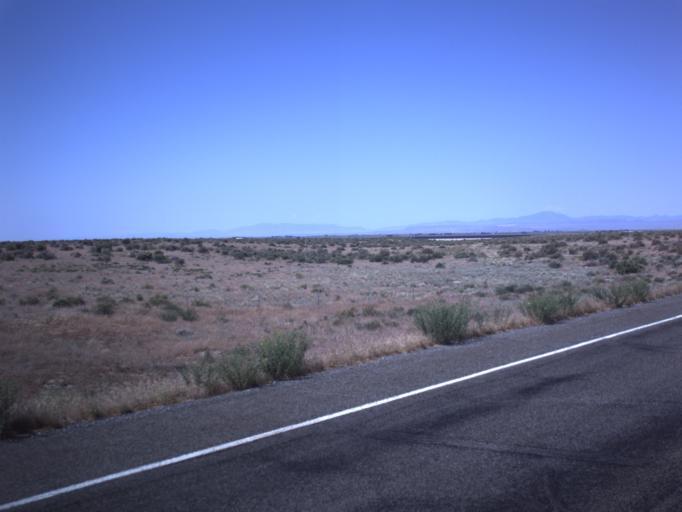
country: US
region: Utah
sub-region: Millard County
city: Delta
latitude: 39.4882
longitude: -112.5467
